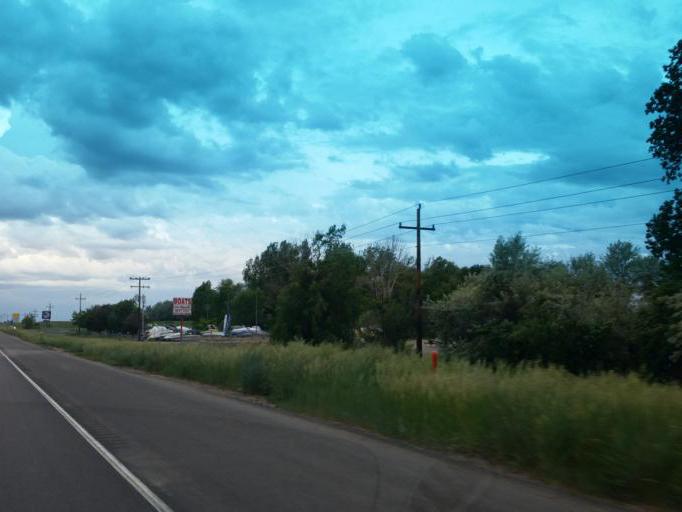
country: US
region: Colorado
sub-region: Weld County
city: Windsor
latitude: 40.5055
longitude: -104.9919
